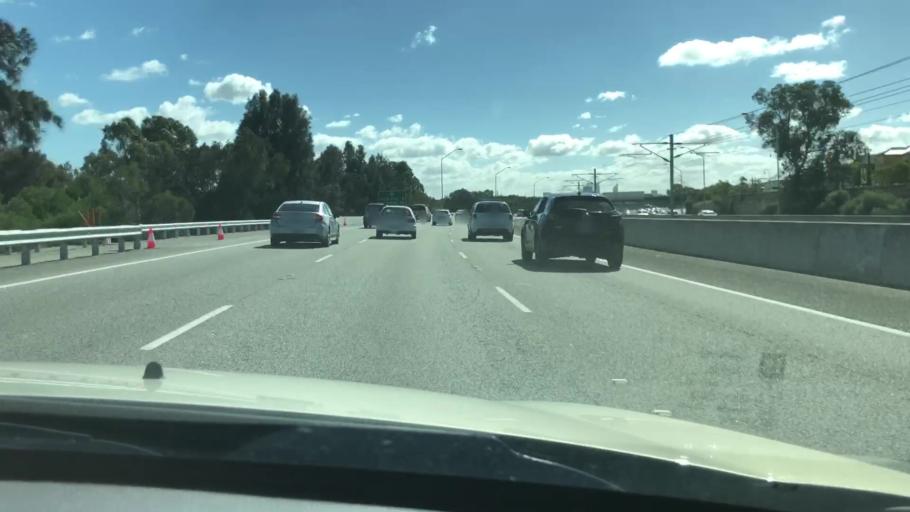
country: AU
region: Western Australia
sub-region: South Perth
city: Manning
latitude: -32.0211
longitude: 115.8575
